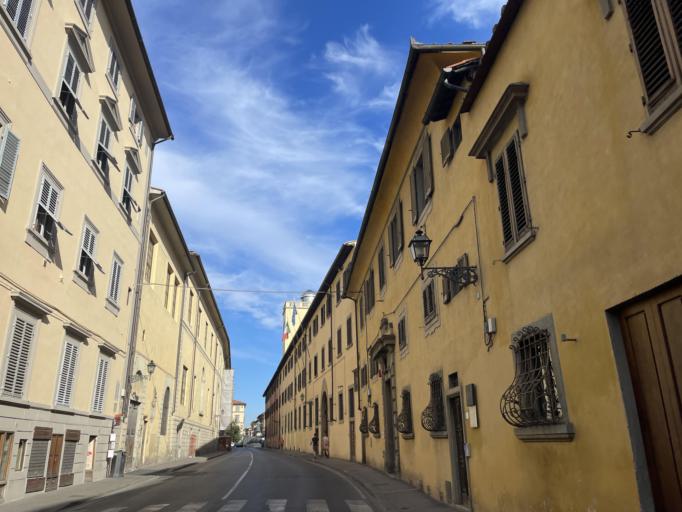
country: IT
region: Tuscany
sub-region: Province of Florence
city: Florence
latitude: 43.7769
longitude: 11.2607
